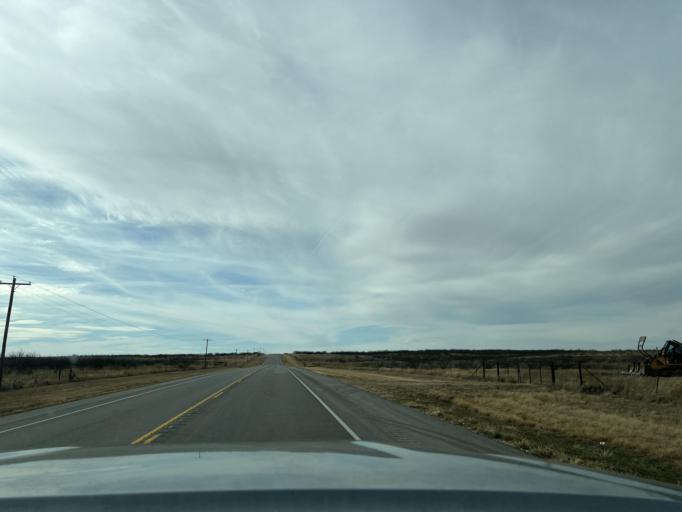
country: US
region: Texas
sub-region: Jones County
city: Anson
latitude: 32.7504
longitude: -99.6604
